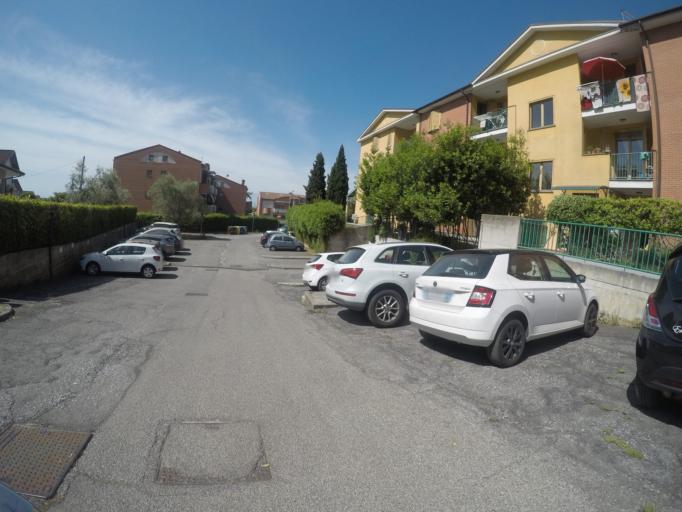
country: IT
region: Tuscany
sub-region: Provincia di Massa-Carrara
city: Massa
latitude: 44.0407
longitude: 10.0959
